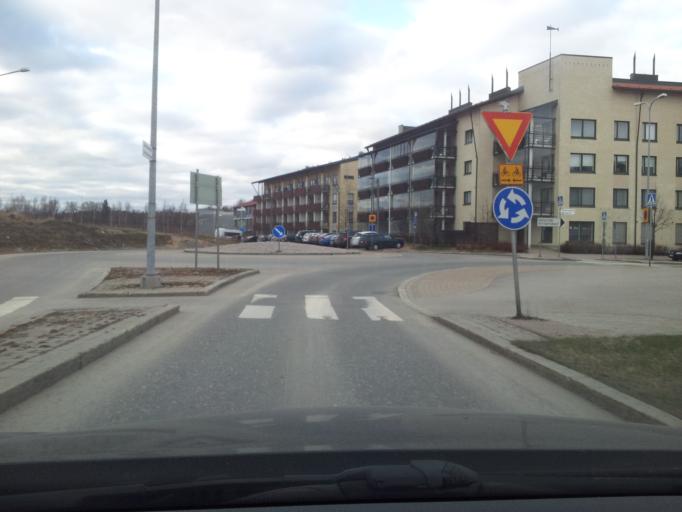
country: FI
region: Uusimaa
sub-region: Helsinki
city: Kilo
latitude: 60.2171
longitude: 24.8007
